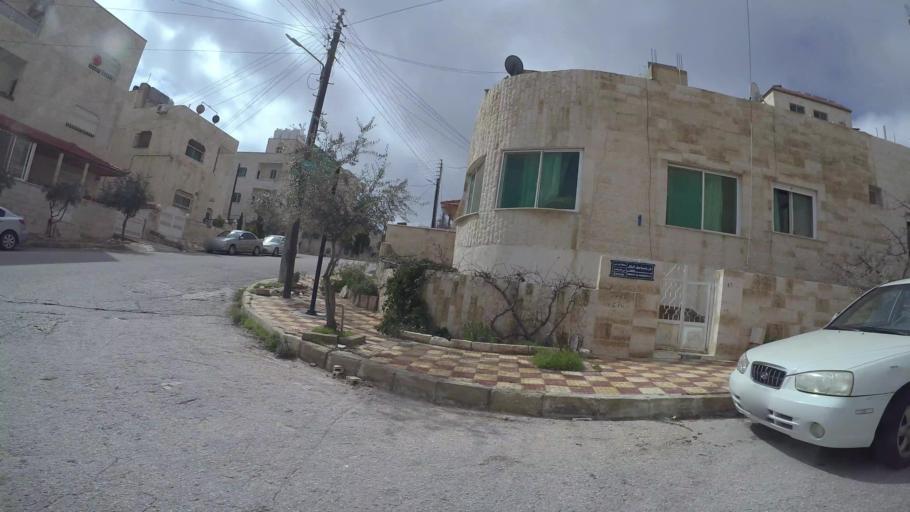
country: JO
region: Amman
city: Al Jubayhah
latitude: 32.0652
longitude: 35.8816
